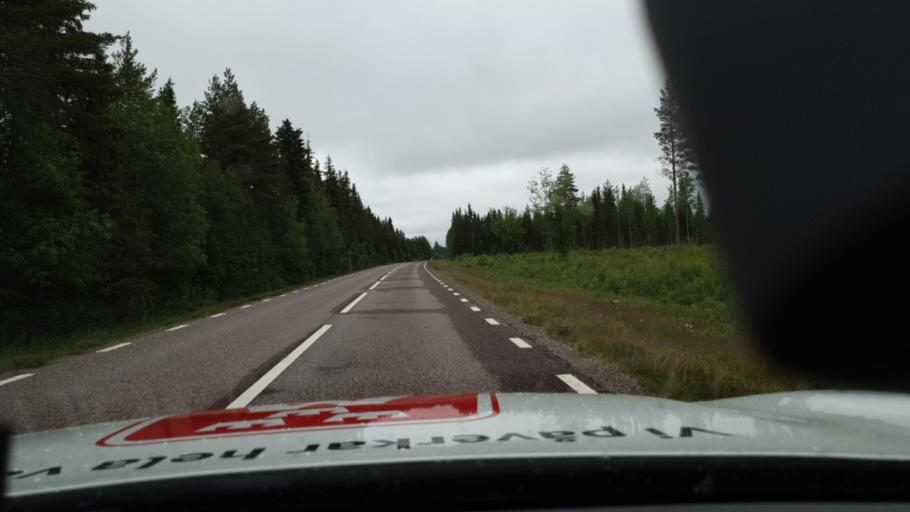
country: FI
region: Lapland
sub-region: Torniolaakso
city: Pello
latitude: 66.9226
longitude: 23.8523
